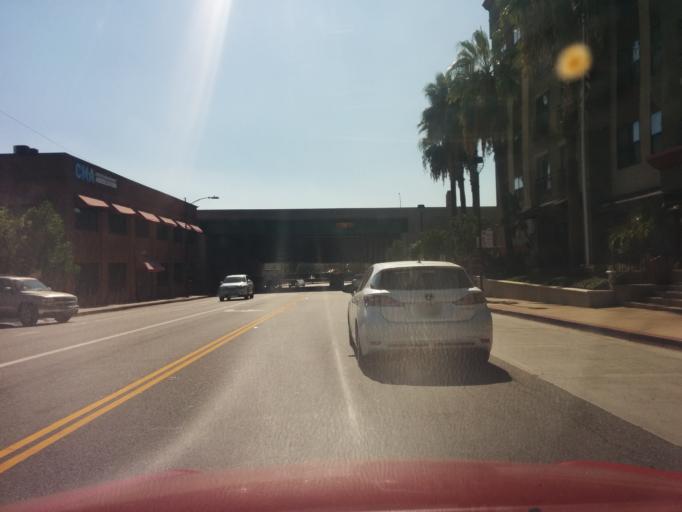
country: US
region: California
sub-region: Los Angeles County
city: Burbank
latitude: 34.1774
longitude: -118.3072
